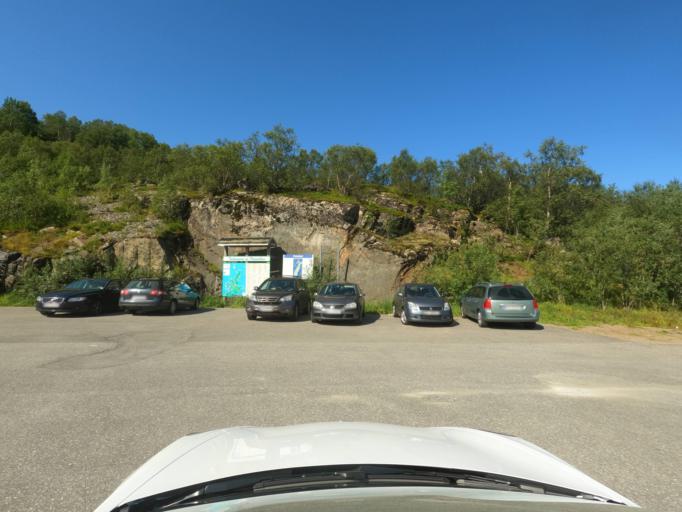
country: NO
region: Nordland
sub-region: Hadsel
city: Melbu
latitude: 68.4310
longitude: 14.8240
